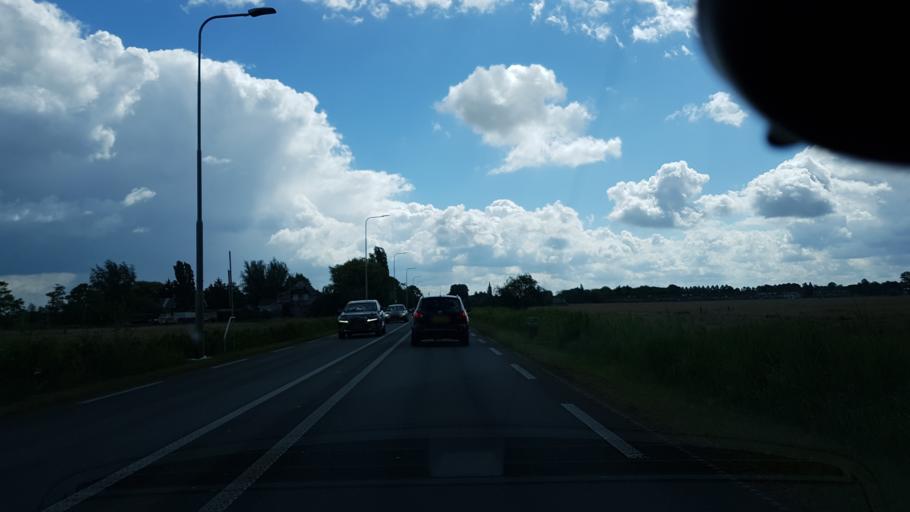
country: NL
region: Utrecht
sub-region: Gemeente De Ronde Venen
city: Mijdrecht
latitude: 52.2162
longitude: 4.9087
